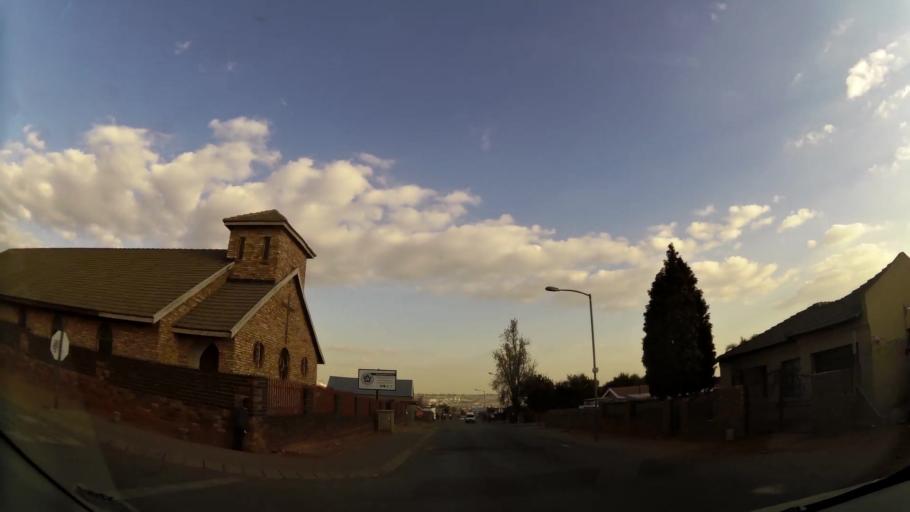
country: ZA
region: Gauteng
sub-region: West Rand District Municipality
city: Krugersdorp
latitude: -26.0737
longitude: 27.7585
